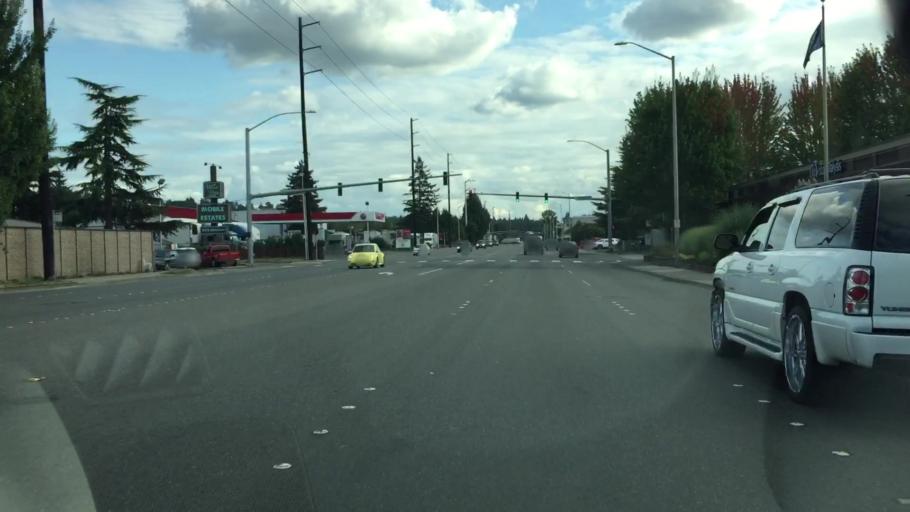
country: US
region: Washington
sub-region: King County
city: Kent
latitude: 47.4055
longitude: -122.2281
